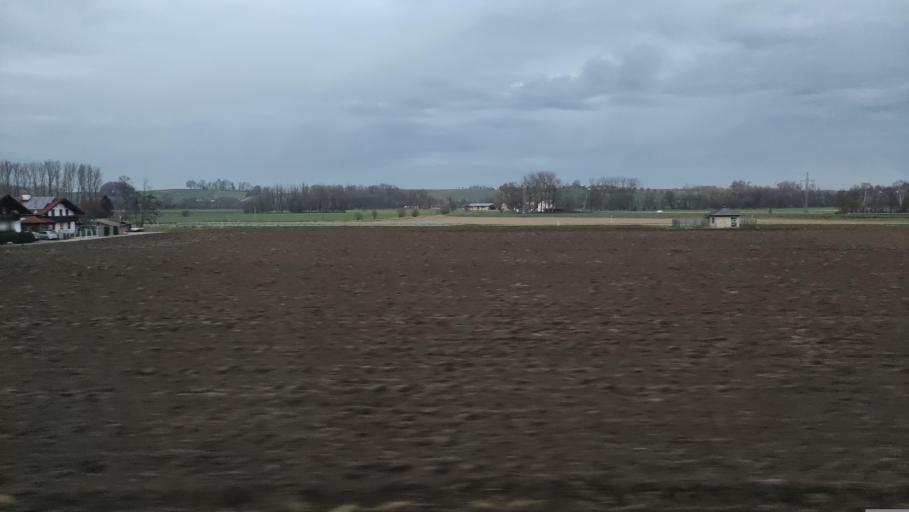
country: DE
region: Bavaria
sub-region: Upper Bavaria
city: Rattenkirchen
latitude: 48.2549
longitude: 12.3457
